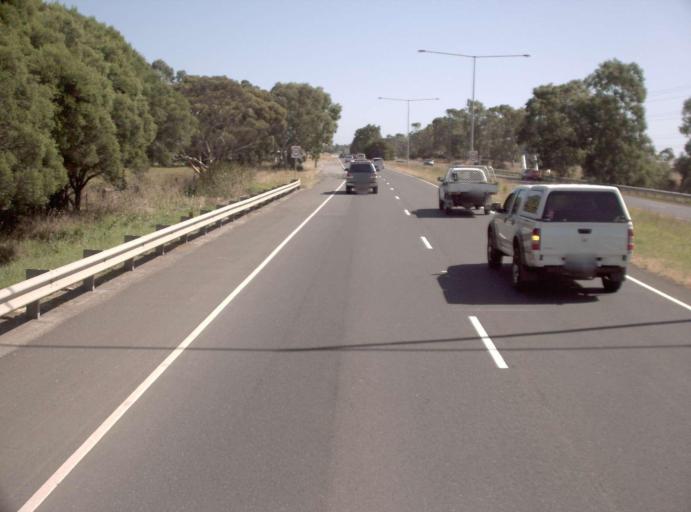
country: AU
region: Victoria
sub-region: Frankston
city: Sandhurst
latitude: -38.0730
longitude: 145.1942
